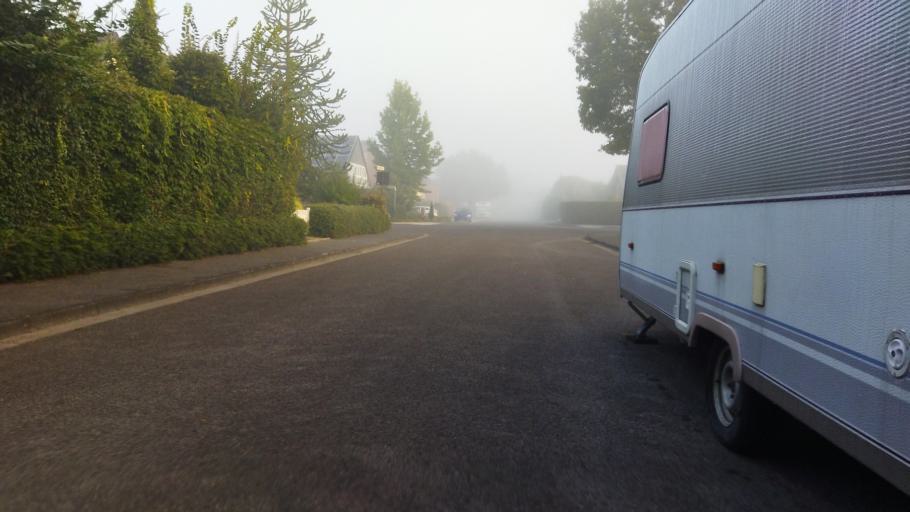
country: DE
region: North Rhine-Westphalia
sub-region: Regierungsbezirk Munster
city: Steinfurt
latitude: 52.1338
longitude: 7.3272
